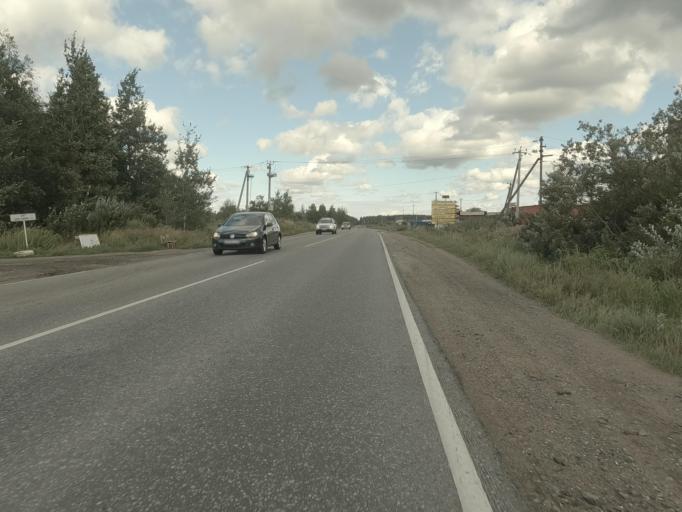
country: RU
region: Leningrad
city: Shcheglovo
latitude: 60.0292
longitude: 30.7762
